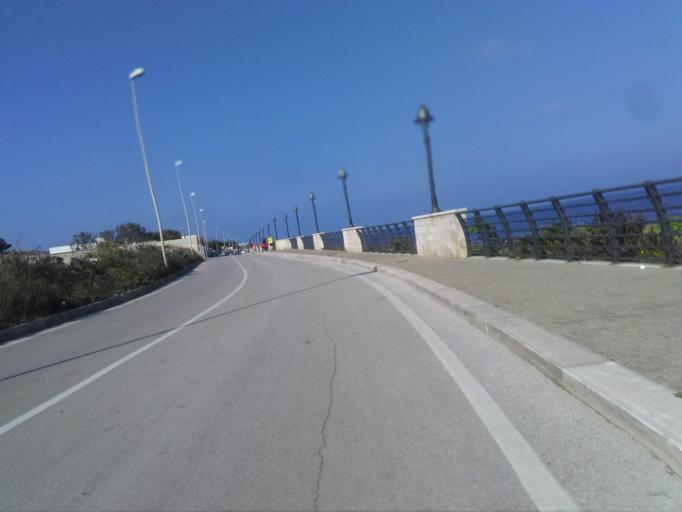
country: IT
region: Apulia
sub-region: Provincia di Bari
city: San Paolo
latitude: 41.1536
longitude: 16.7861
